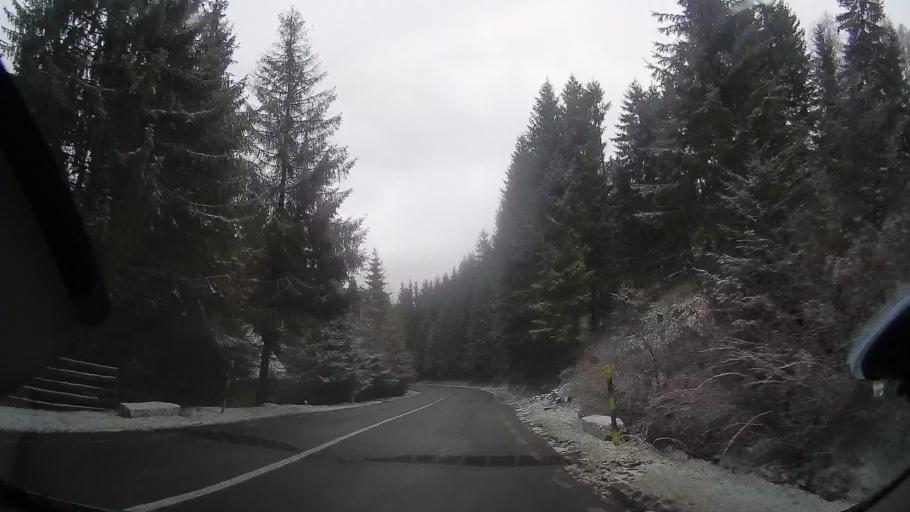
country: RO
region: Cluj
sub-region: Comuna Calatele
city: Calatele
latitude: 46.7190
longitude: 23.0429
